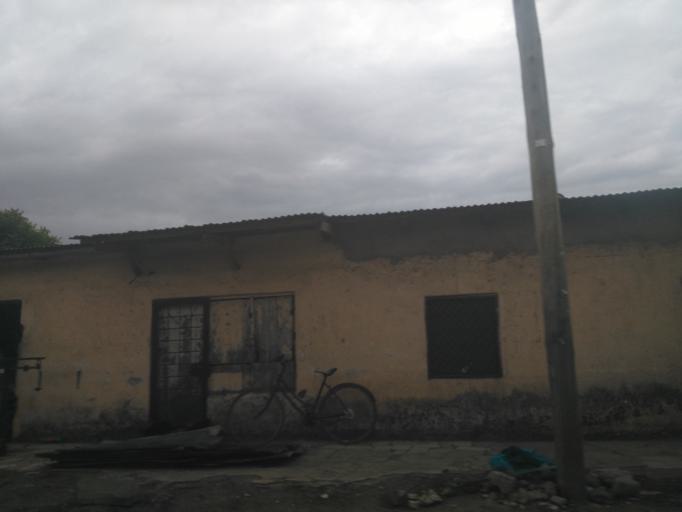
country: TZ
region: Dar es Salaam
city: Magomeni
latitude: -6.7959
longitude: 39.2667
